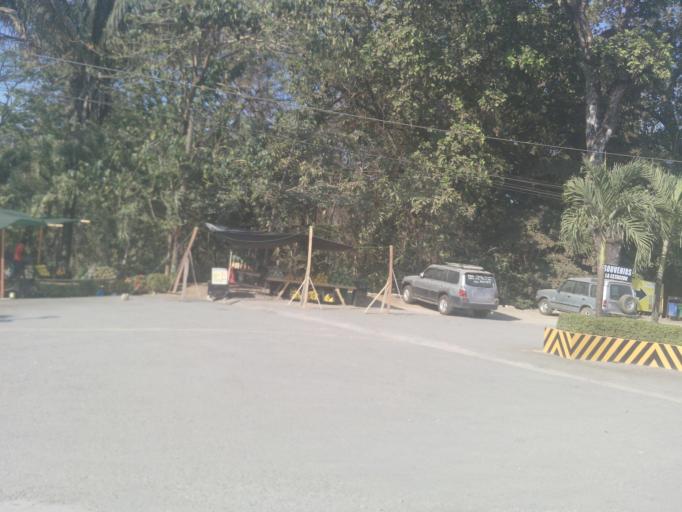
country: CR
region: Guanacaste
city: Samara
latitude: 9.9636
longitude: -85.6644
